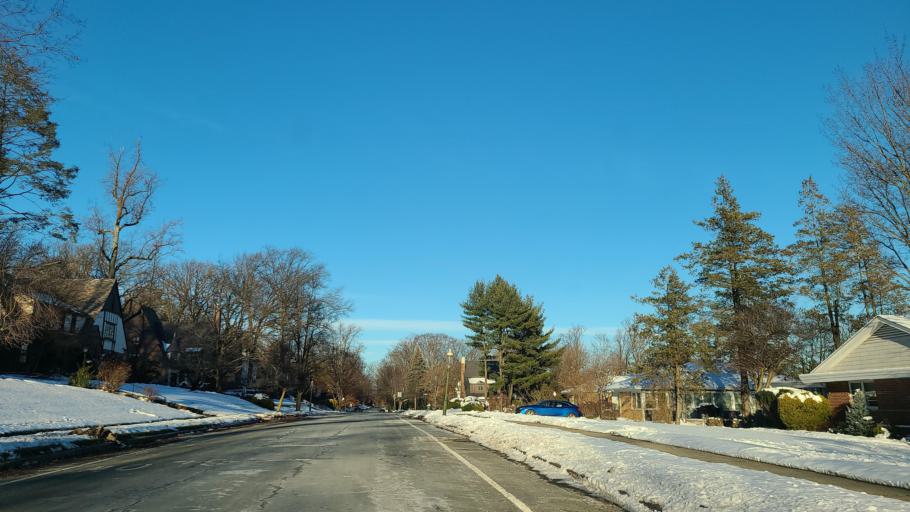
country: US
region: New Jersey
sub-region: Essex County
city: South Orange
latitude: 40.7489
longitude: -74.2732
